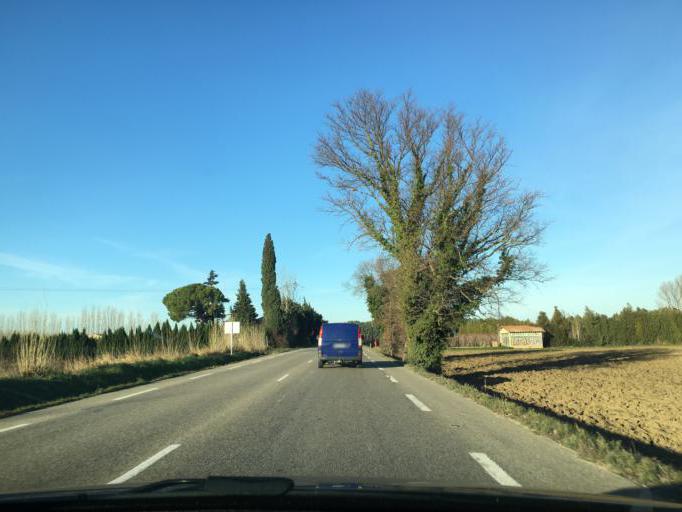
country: FR
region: Provence-Alpes-Cote d'Azur
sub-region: Departement du Vaucluse
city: Le Thor
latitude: 43.8840
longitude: 4.9940
